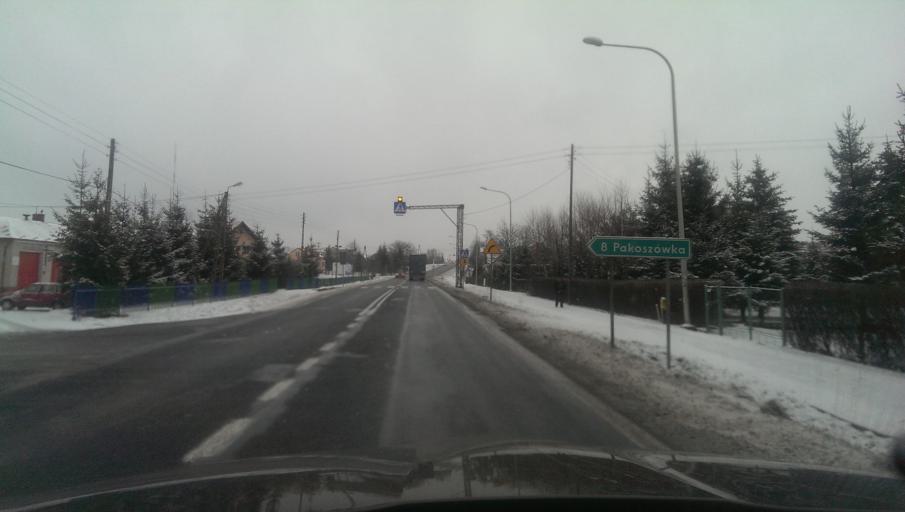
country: PL
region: Subcarpathian Voivodeship
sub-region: Powiat sanocki
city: Dlugie
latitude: 49.5780
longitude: 22.0434
